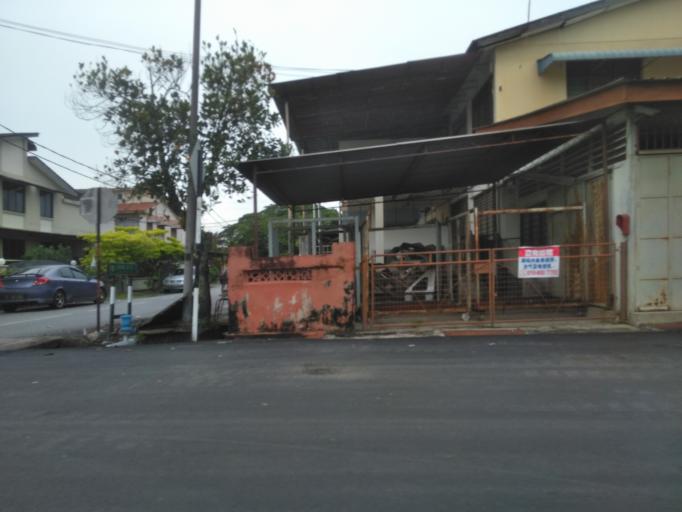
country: MY
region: Penang
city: Bukit Mertajam
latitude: 5.3623
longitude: 100.4502
